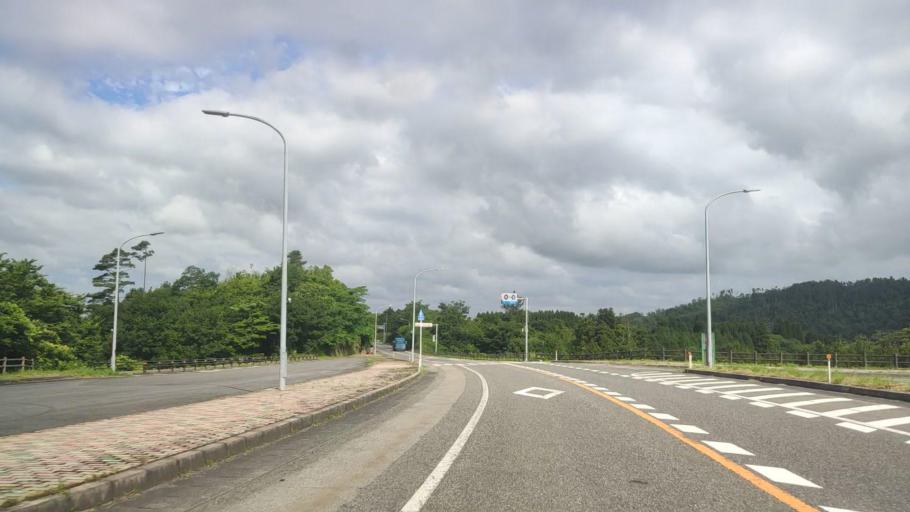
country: JP
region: Tottori
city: Yonago
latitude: 35.4175
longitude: 133.4581
